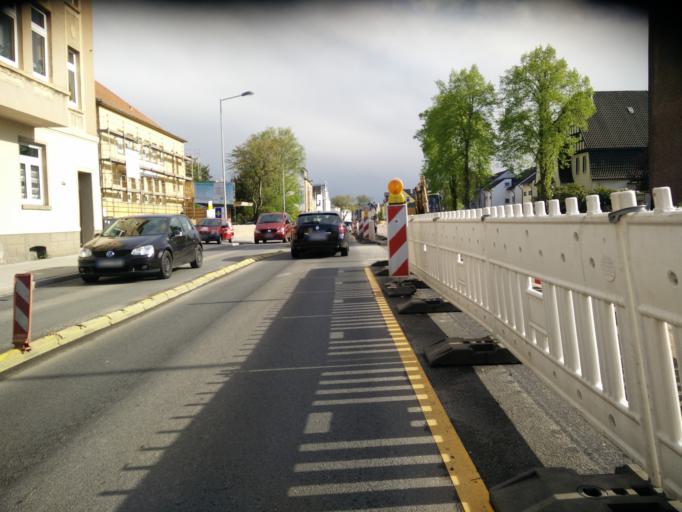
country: DE
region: North Rhine-Westphalia
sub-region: Regierungsbezirk Arnsberg
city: Bochum
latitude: 51.5079
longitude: 7.2117
